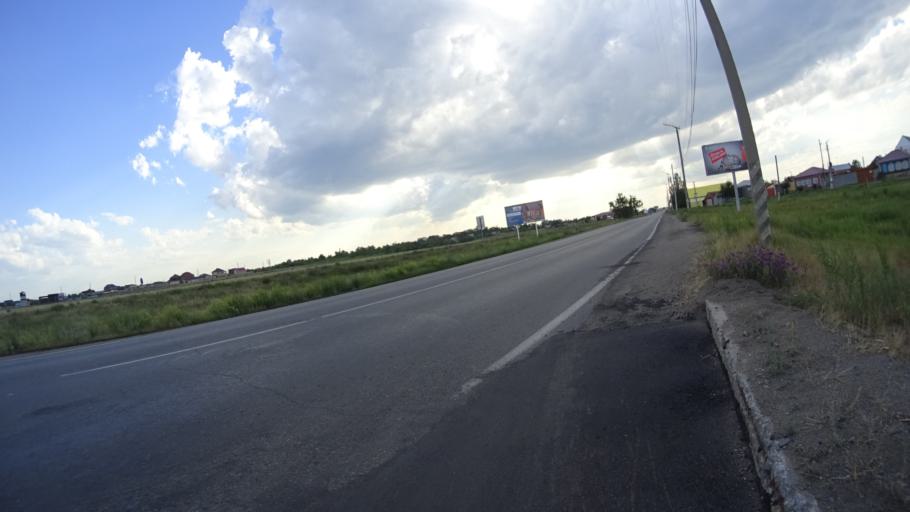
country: RU
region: Chelyabinsk
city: Troitsk
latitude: 54.0824
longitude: 61.5178
